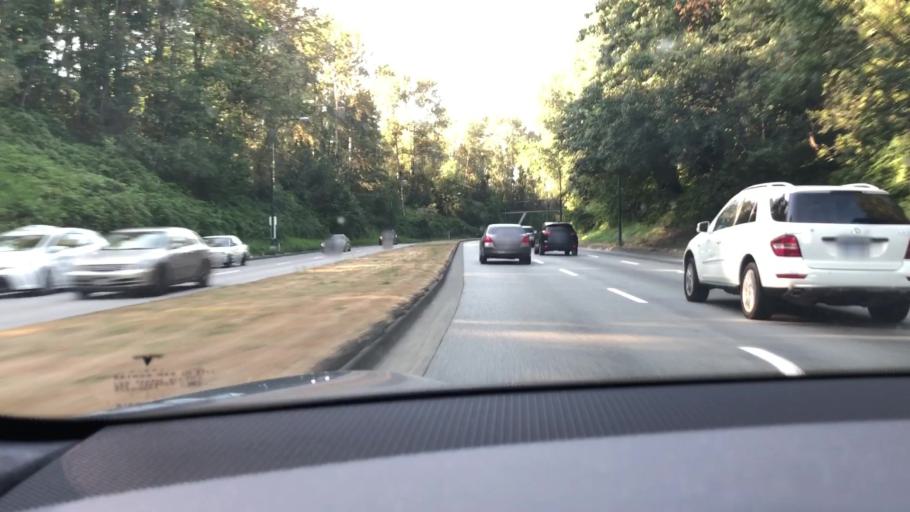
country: CA
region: British Columbia
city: Burnaby
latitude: 49.2092
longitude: -123.0237
